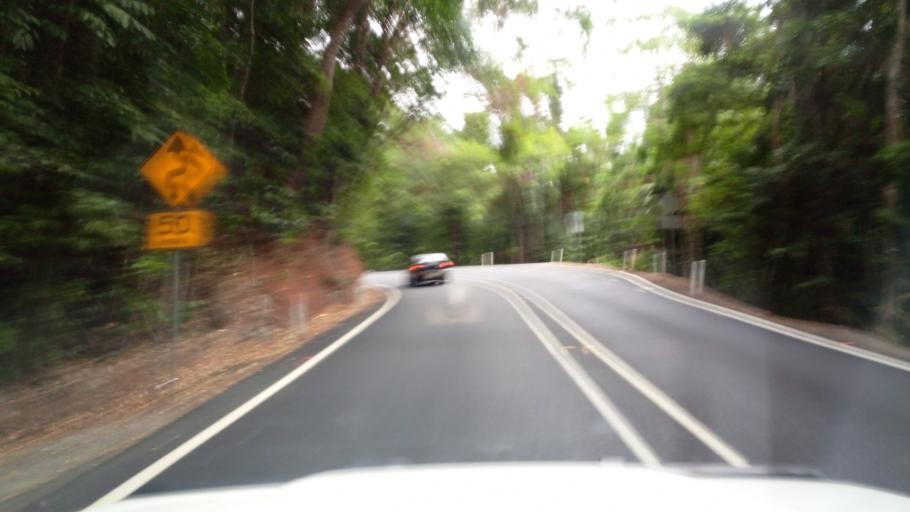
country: AU
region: Queensland
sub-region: Tablelands
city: Kuranda
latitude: -16.8426
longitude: 145.6729
